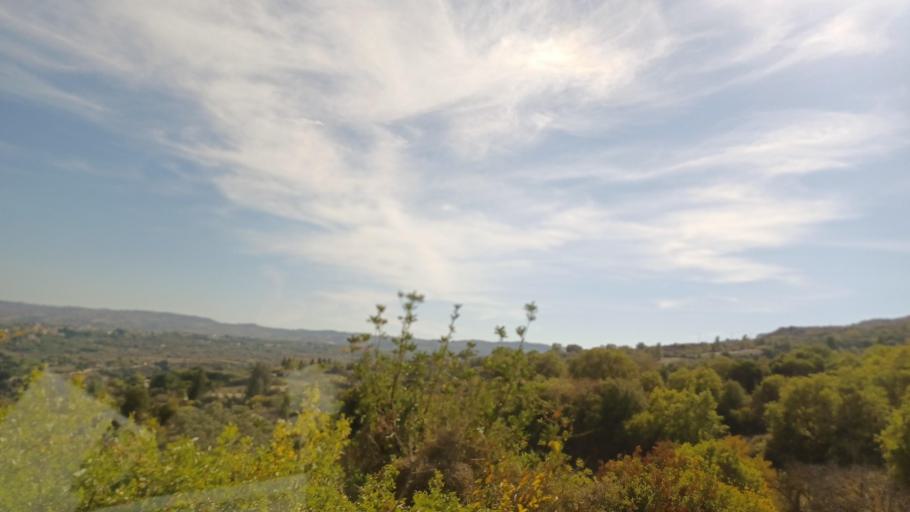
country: CY
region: Pafos
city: Pegeia
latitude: 34.9403
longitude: 32.4560
